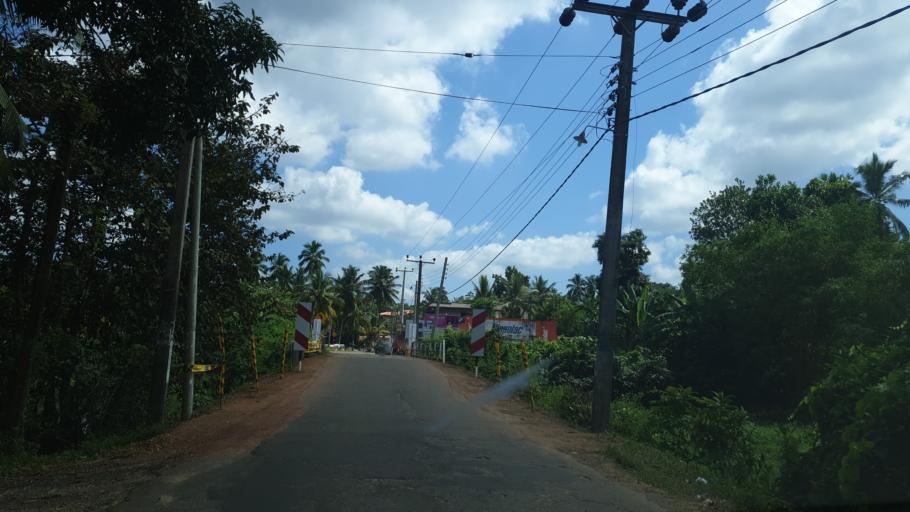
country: LK
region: Western
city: Panadura
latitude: 6.6655
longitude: 79.9577
